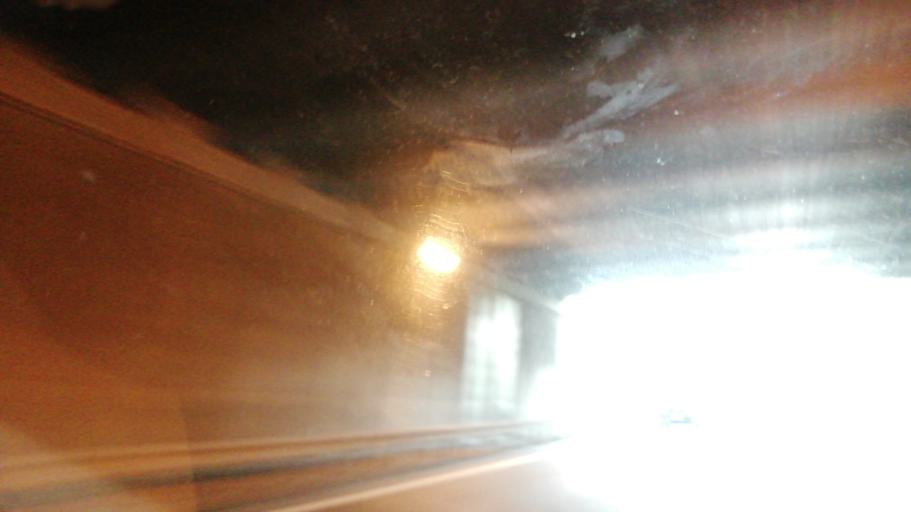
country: TR
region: Istanbul
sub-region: Atasehir
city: Atasehir
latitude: 40.9956
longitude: 29.1235
